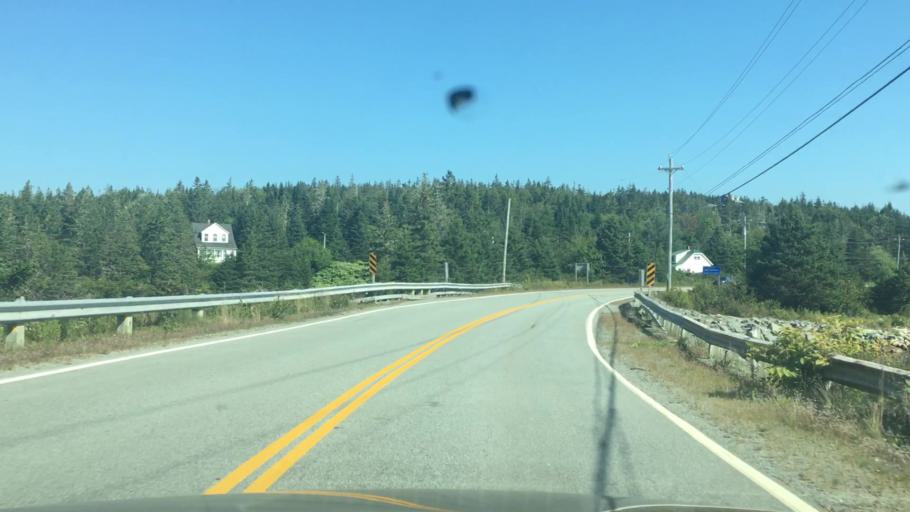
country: CA
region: Nova Scotia
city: New Glasgow
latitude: 44.8216
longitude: -62.6346
